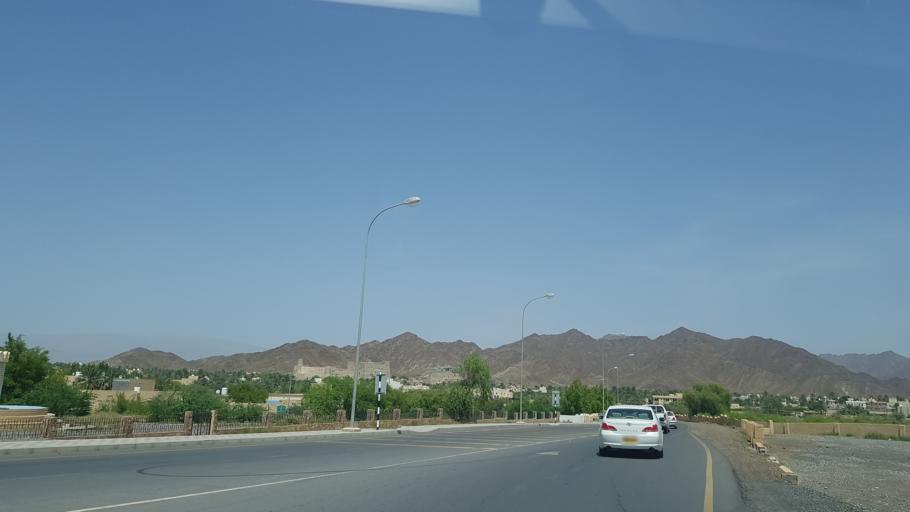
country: OM
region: Muhafazat ad Dakhiliyah
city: Bahla'
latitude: 22.9591
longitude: 57.2939
